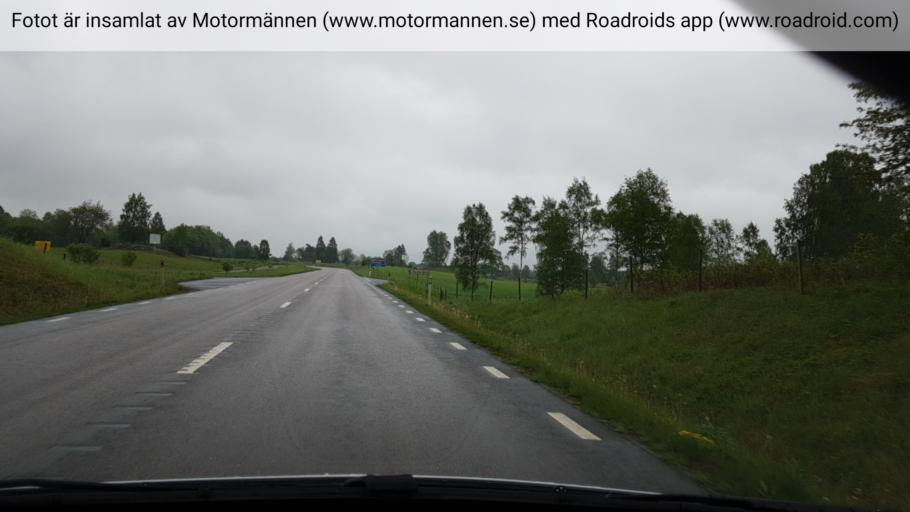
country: SE
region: Vaestra Goetaland
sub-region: Falkopings Kommun
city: Falkoeping
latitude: 58.0085
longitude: 13.5661
